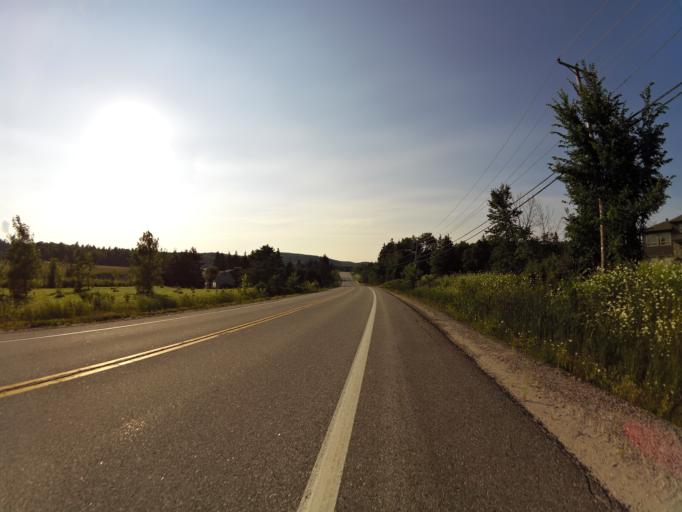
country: CA
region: Quebec
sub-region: Outaouais
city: Wakefield
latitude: 45.5949
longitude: -75.8940
